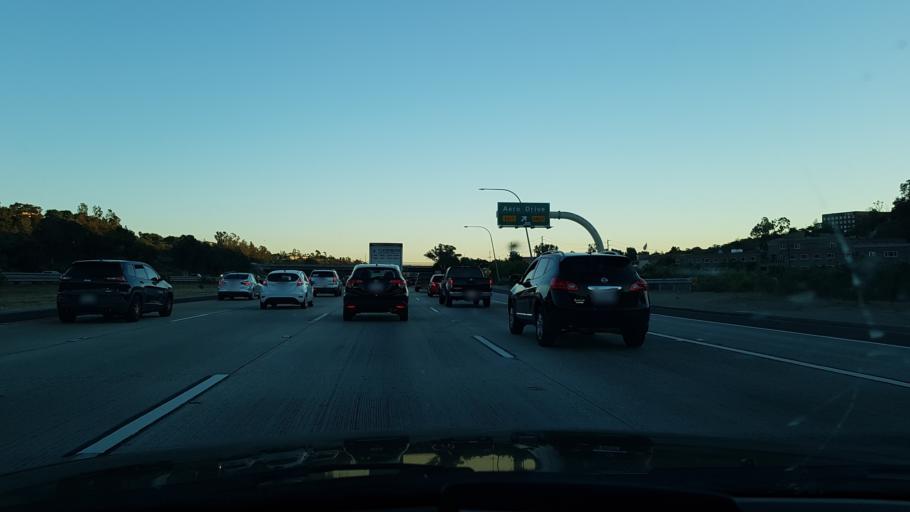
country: US
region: California
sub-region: San Diego County
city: La Mesa
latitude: 32.8141
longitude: -117.1149
